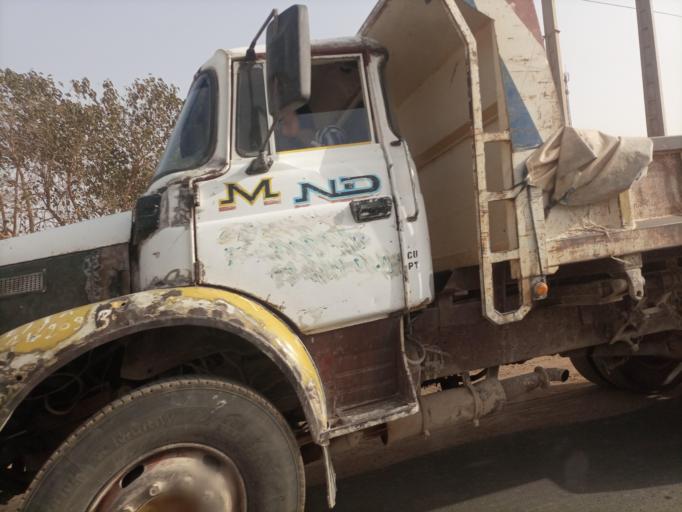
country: SN
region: Thies
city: Nguekhokh
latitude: 14.5839
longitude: -17.0320
